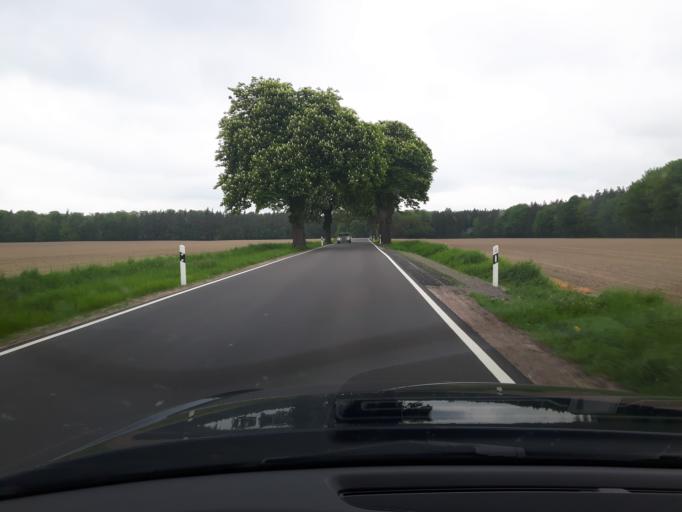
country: DE
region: Mecklenburg-Vorpommern
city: Gnoien
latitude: 53.9970
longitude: 12.6794
